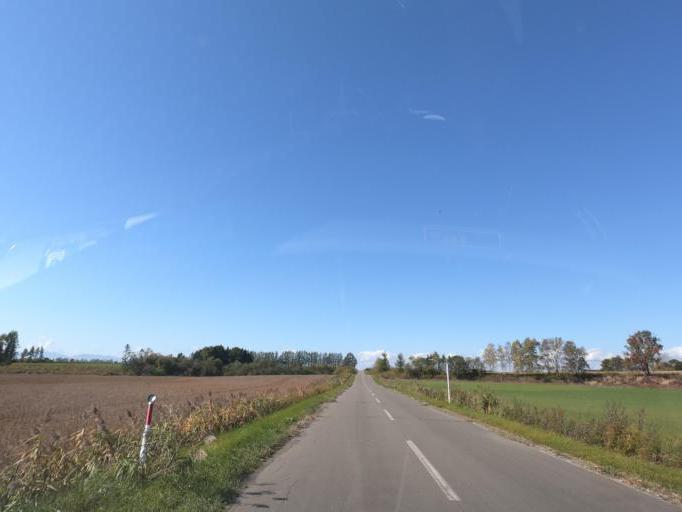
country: JP
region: Hokkaido
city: Otofuke
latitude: 43.0595
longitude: 143.2759
